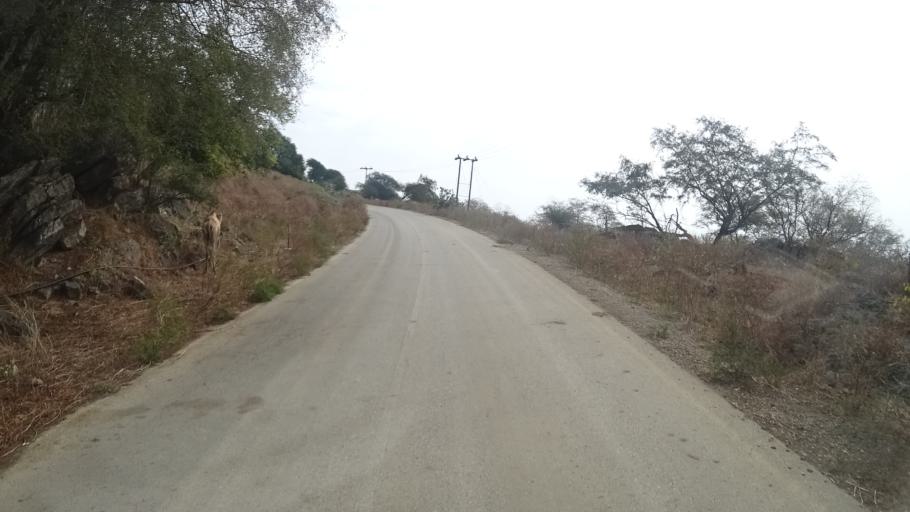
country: YE
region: Al Mahrah
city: Hawf
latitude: 16.7104
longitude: 53.2344
